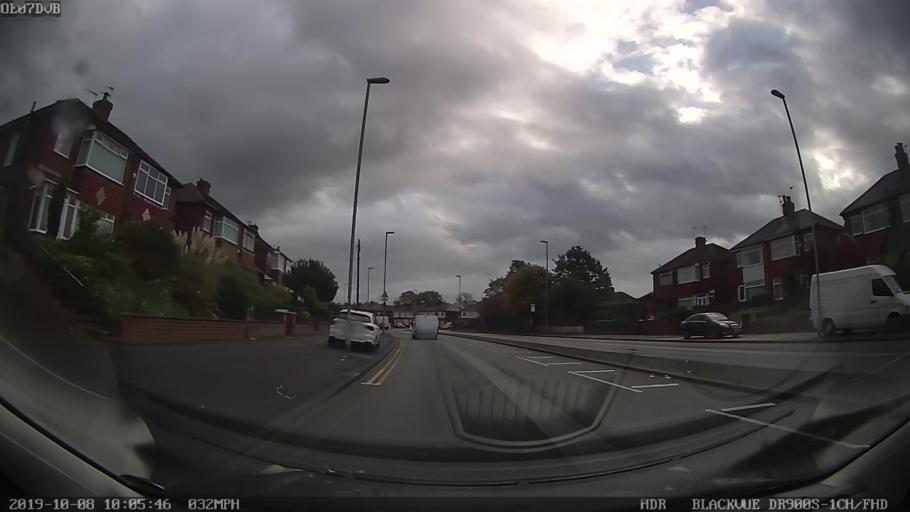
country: GB
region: England
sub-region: Manchester
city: Failsworth
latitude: 53.5217
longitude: -2.1621
